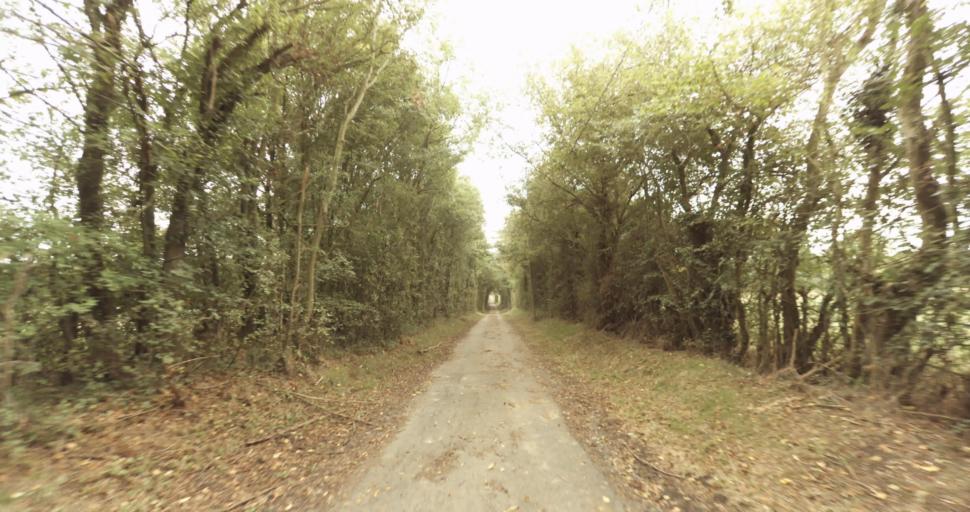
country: FR
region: Lower Normandy
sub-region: Departement de l'Orne
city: Gace
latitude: 48.6883
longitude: 0.2960
